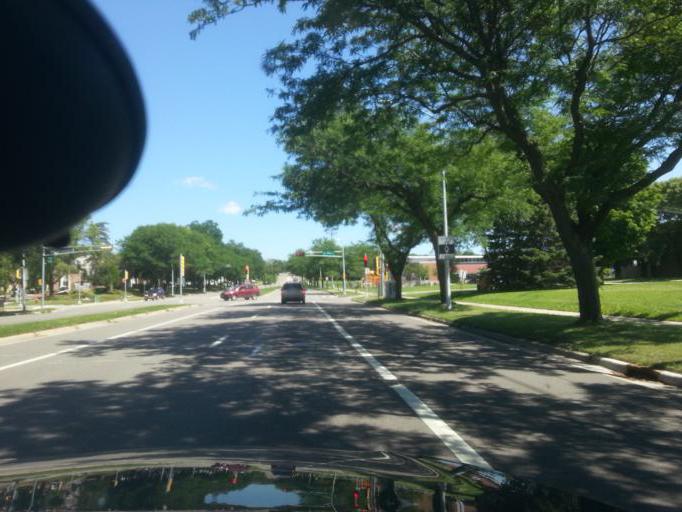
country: US
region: Wisconsin
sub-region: Dane County
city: Middleton
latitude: 43.0649
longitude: -89.5026
